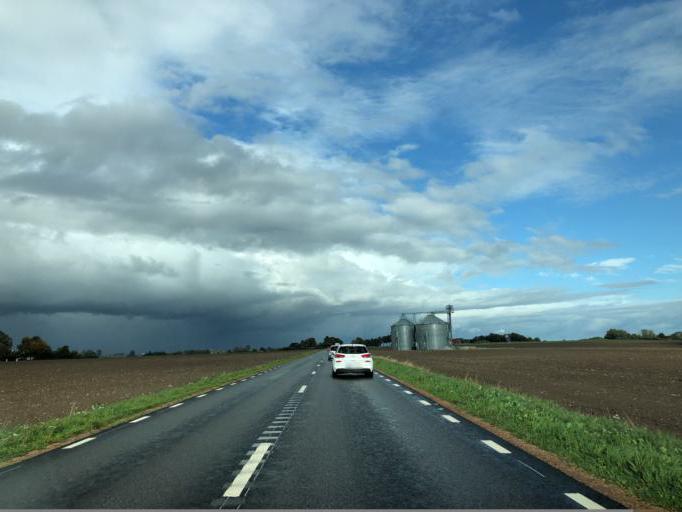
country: SE
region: Skane
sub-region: Kavlinge Kommun
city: Loddekopinge
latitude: 55.7748
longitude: 13.0601
